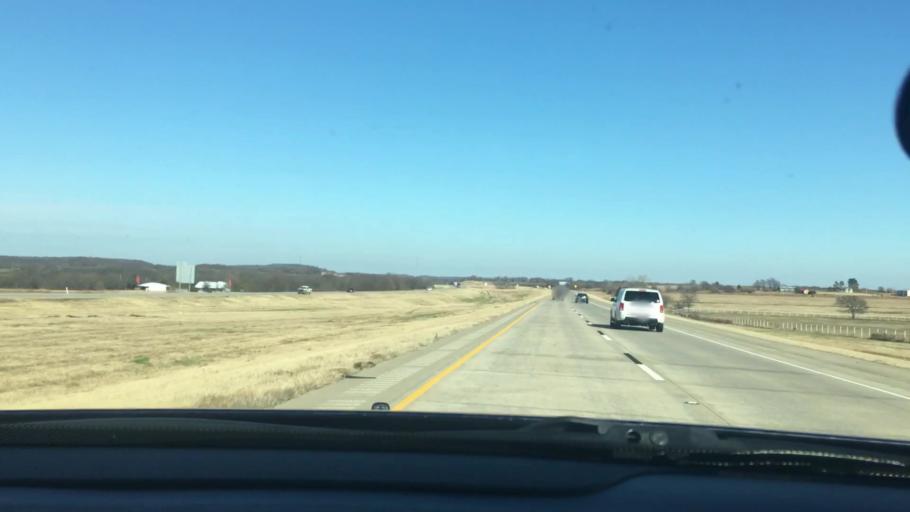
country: US
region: Oklahoma
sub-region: Love County
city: Marietta
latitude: 33.9696
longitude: -97.1341
